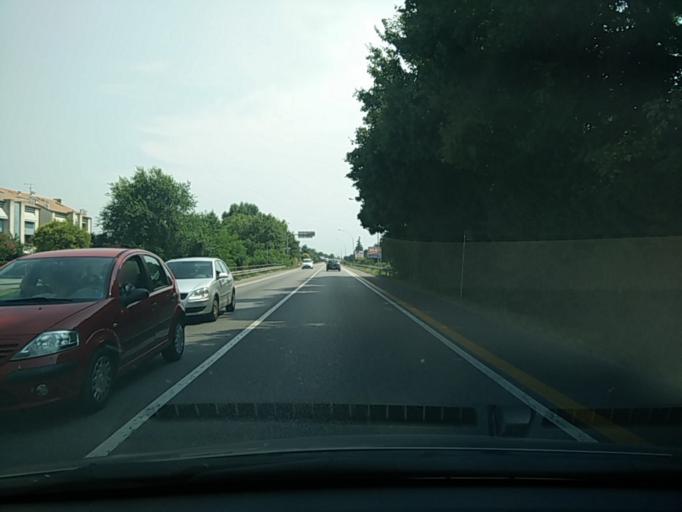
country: IT
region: Veneto
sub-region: Provincia di Treviso
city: Conegliano
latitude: 45.8719
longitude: 12.2962
